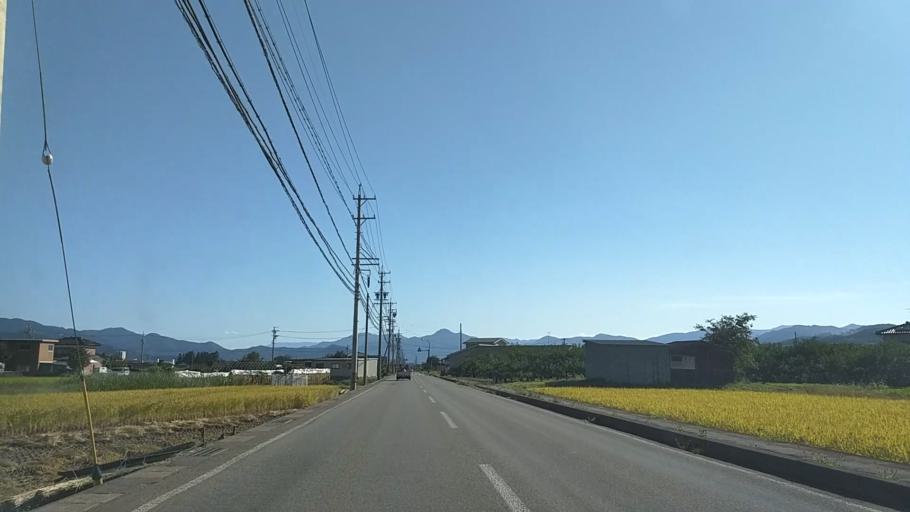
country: JP
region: Nagano
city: Nagano-shi
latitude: 36.6093
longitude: 138.1438
